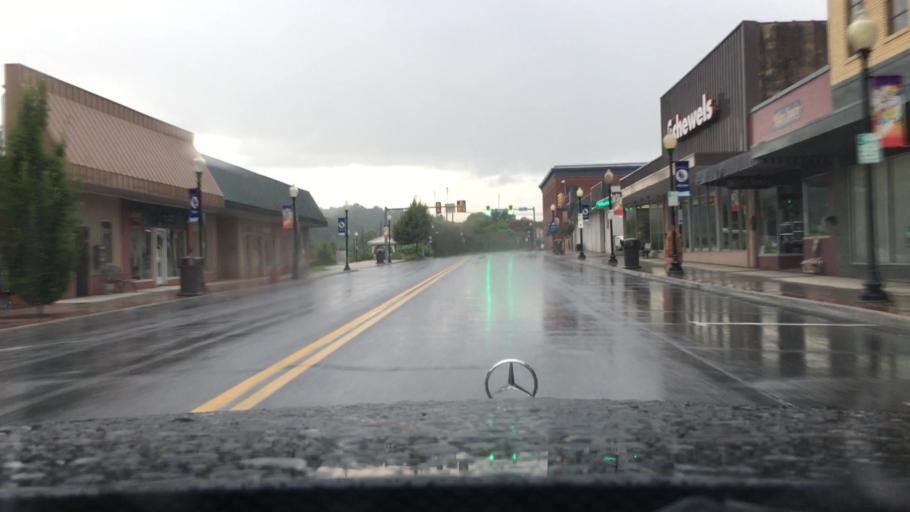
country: US
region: Virginia
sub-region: Campbell County
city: Altavista
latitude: 37.1093
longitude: -79.2890
